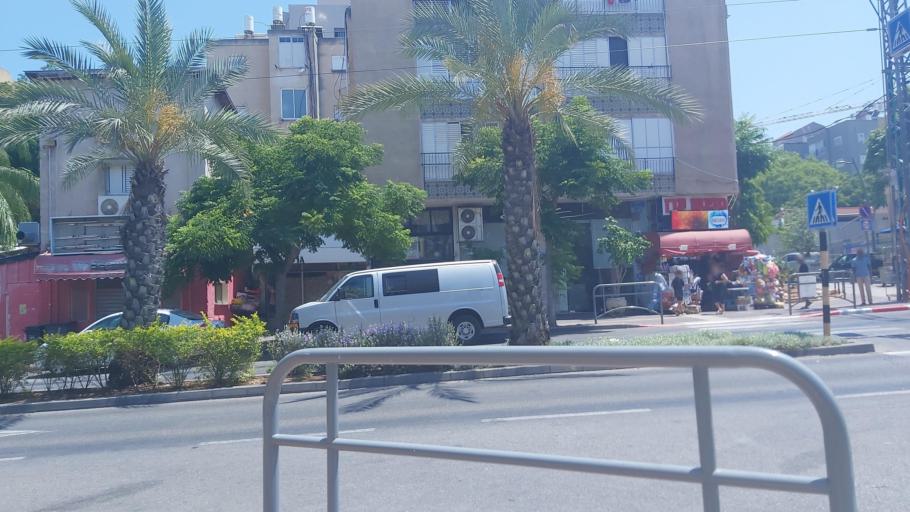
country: IL
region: Central District
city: Rishon LeZiyyon
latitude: 31.9622
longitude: 34.8095
